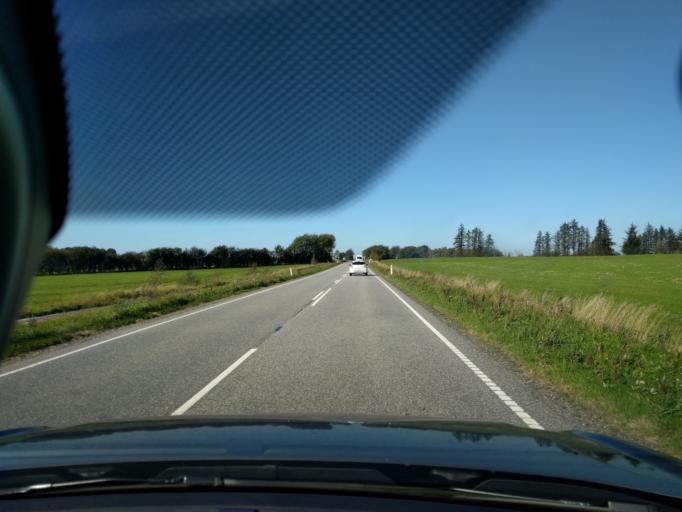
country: DK
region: North Denmark
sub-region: Mariagerfjord Kommune
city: Hobro
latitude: 56.6848
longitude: 9.6580
